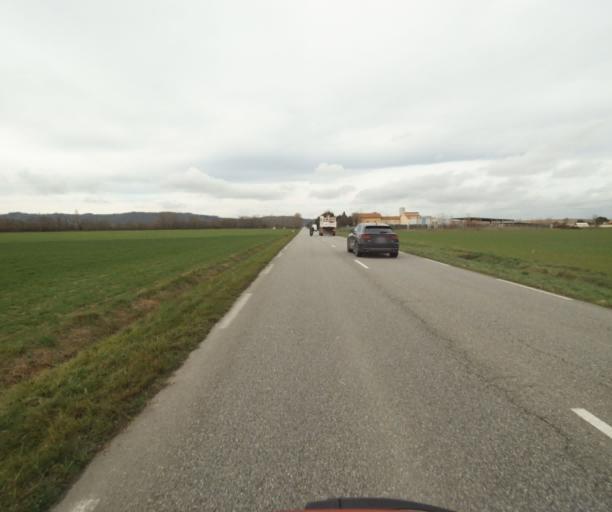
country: FR
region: Midi-Pyrenees
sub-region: Departement de l'Ariege
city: La Tour-du-Crieu
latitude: 43.0988
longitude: 1.6493
